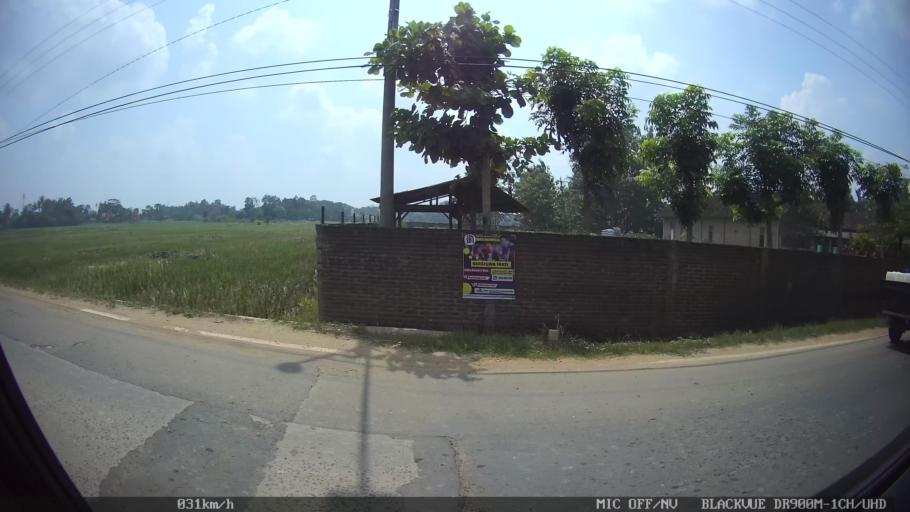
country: ID
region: Lampung
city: Pringsewu
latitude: -5.3733
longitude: 104.9659
